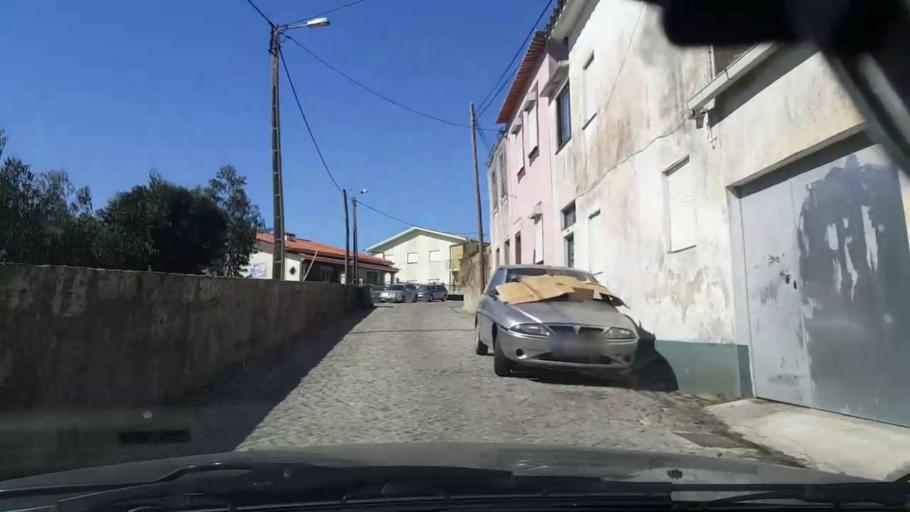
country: PT
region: Porto
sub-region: Vila do Conde
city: Arvore
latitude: 41.3168
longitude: -8.6735
